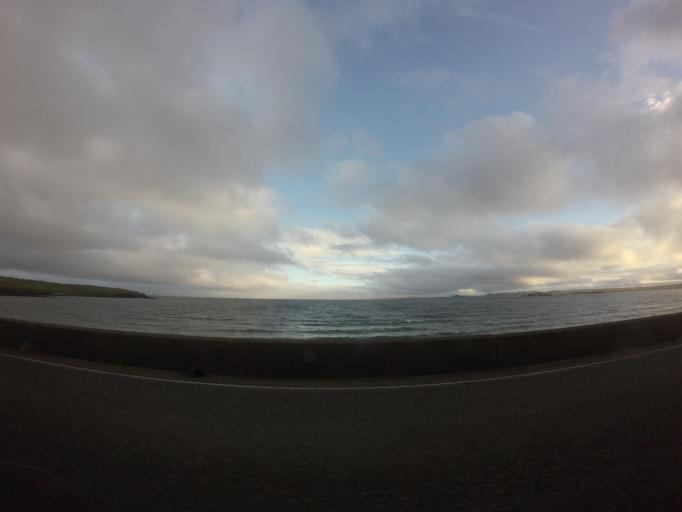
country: GB
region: Scotland
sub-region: Eilean Siar
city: Stornoway
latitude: 58.2062
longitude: -6.2911
